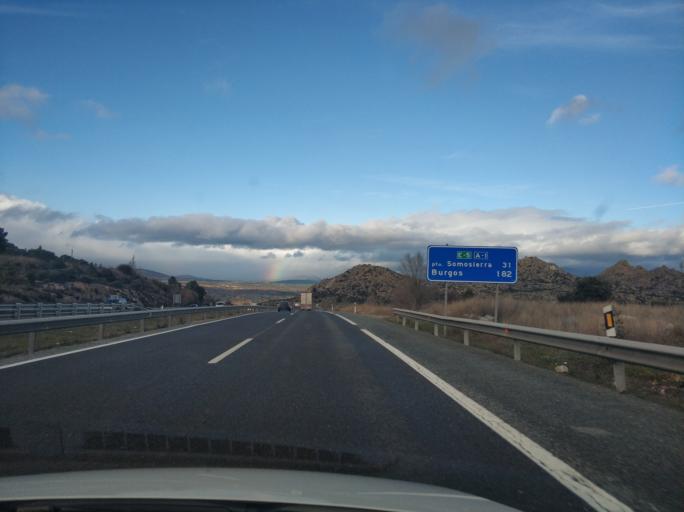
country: ES
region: Madrid
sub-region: Provincia de Madrid
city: La Cabrera
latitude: 40.8782
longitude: -3.5994
